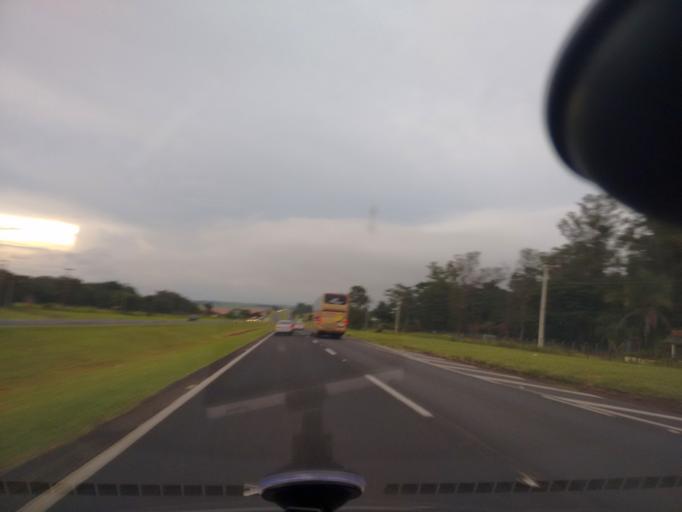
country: BR
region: Sao Paulo
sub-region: Ibate
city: Ibate
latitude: -21.9748
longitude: -47.9371
